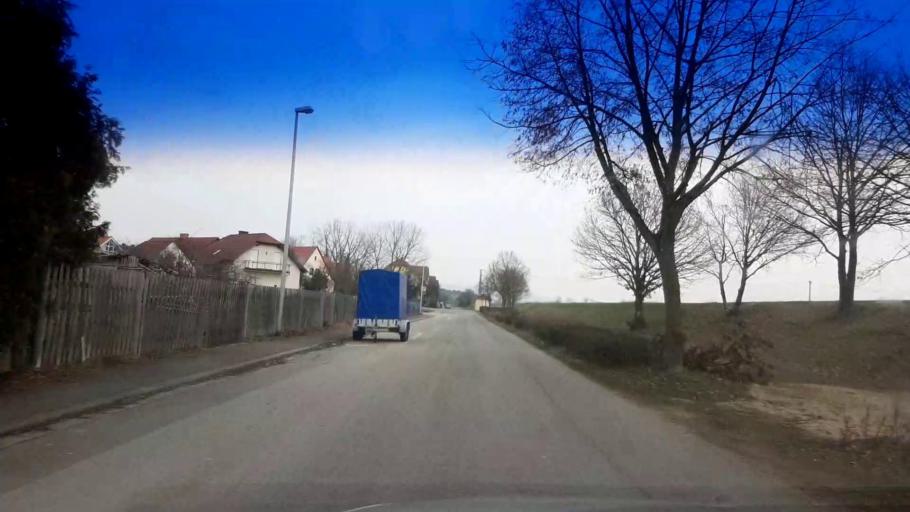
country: DE
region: Bavaria
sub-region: Upper Franconia
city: Hirschaid
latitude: 49.8125
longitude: 10.9894
